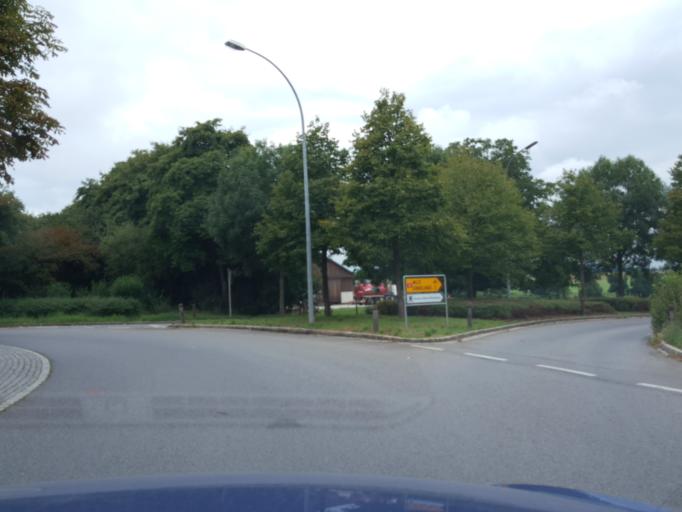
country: LU
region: Luxembourg
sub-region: Canton de Capellen
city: Kehlen
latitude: 49.6782
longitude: 6.0439
